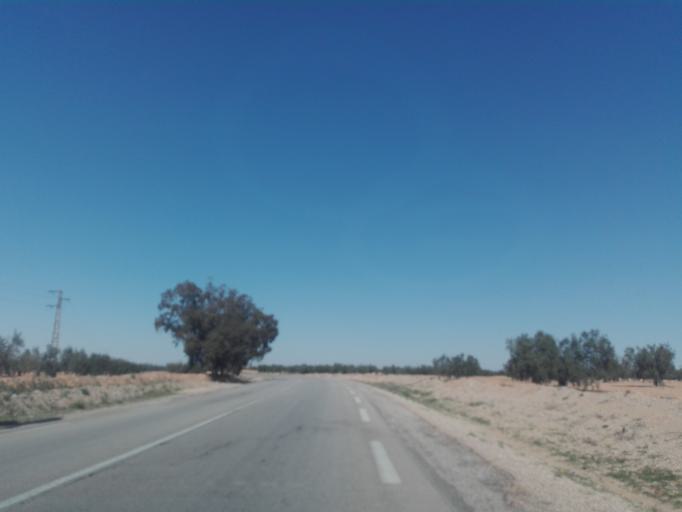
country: TN
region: Safaqis
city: Bi'r `Ali Bin Khalifah
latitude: 34.7563
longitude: 10.3287
